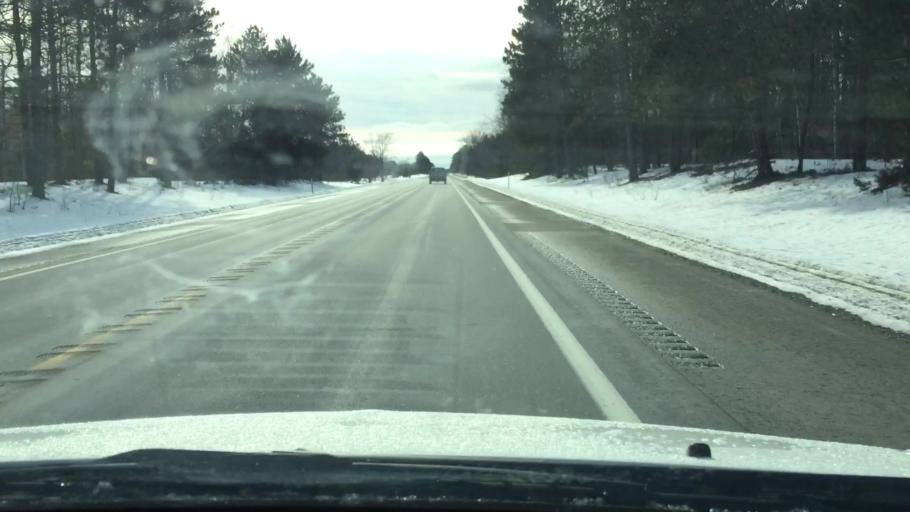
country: US
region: Michigan
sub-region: Kalkaska County
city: Kalkaska
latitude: 44.6925
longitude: -85.2135
